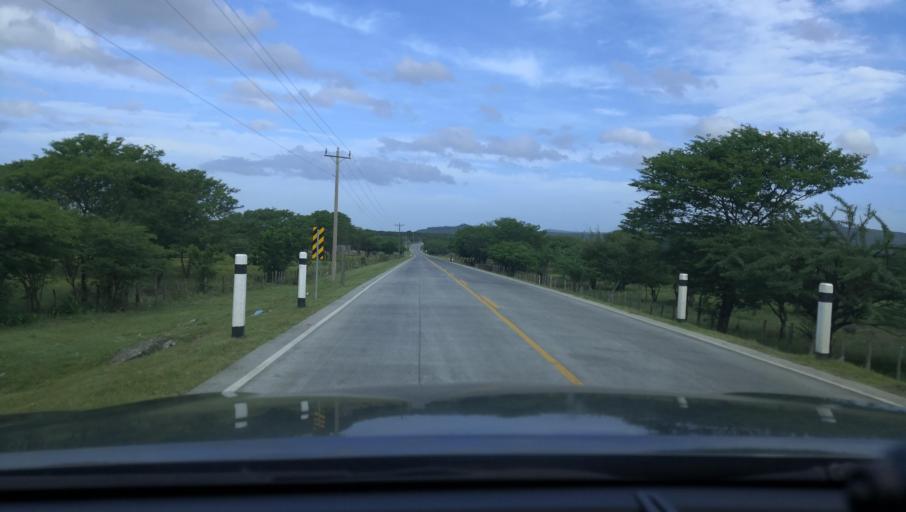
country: NI
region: Boaco
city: San Lorenzo
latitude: 12.1967
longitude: -85.6785
